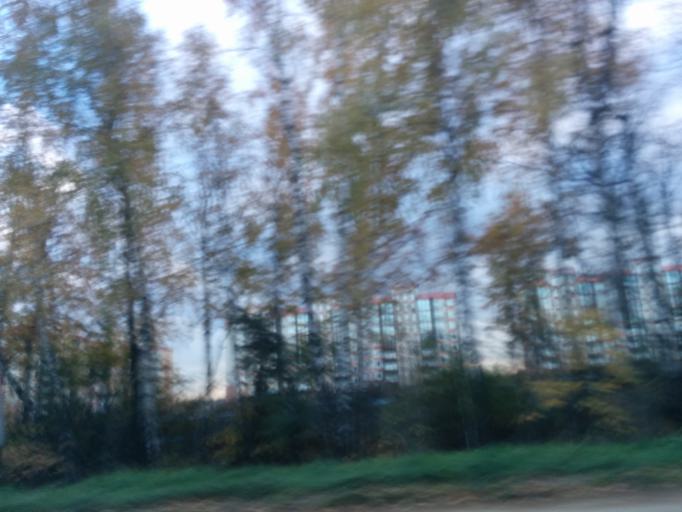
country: RU
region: Moscow
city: Zagor'ye
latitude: 55.5361
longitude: 37.6420
